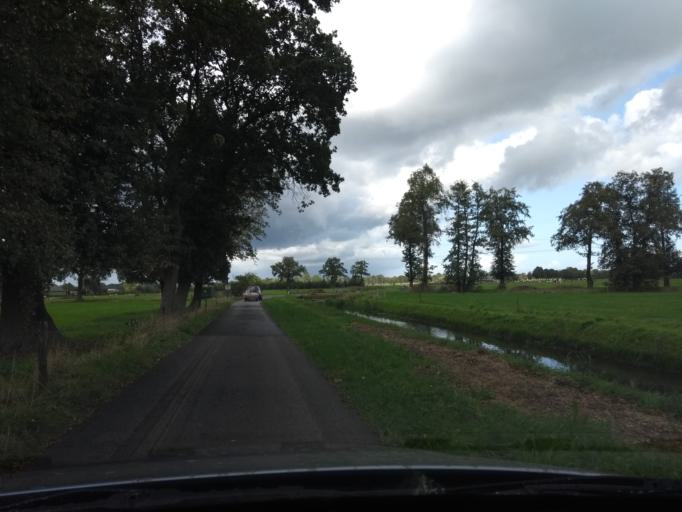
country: NL
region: Overijssel
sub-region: Gemeente Raalte
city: Raalte
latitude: 52.3680
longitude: 6.3360
